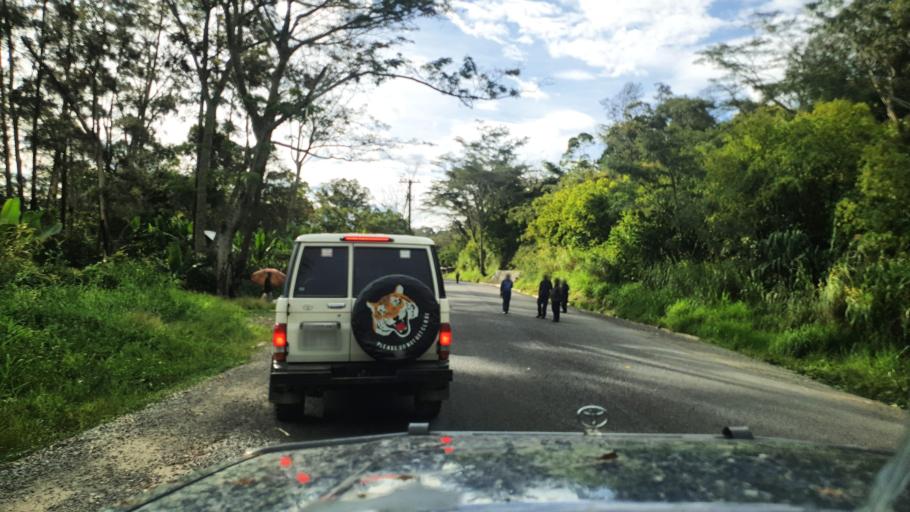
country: PG
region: Jiwaka
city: Minj
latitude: -5.8875
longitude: 144.7317
